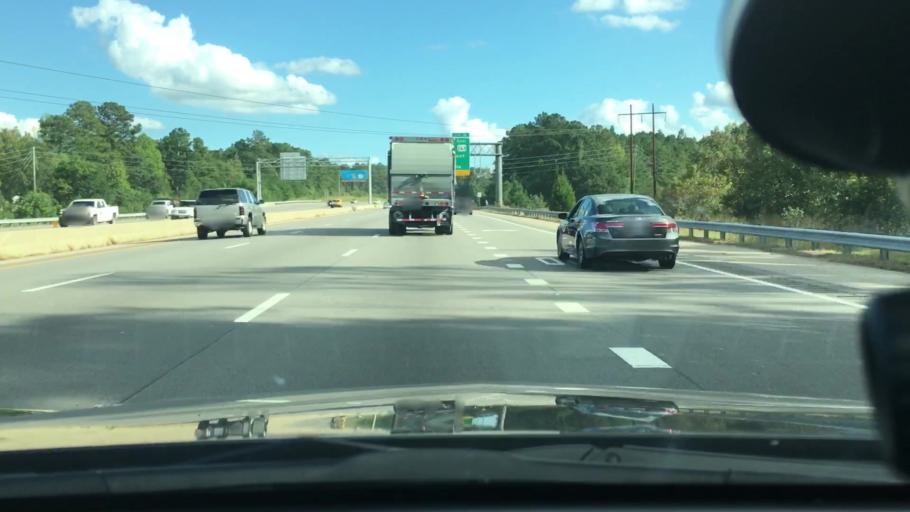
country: US
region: North Carolina
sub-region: Wake County
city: Raleigh
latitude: 35.7912
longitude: -78.5781
